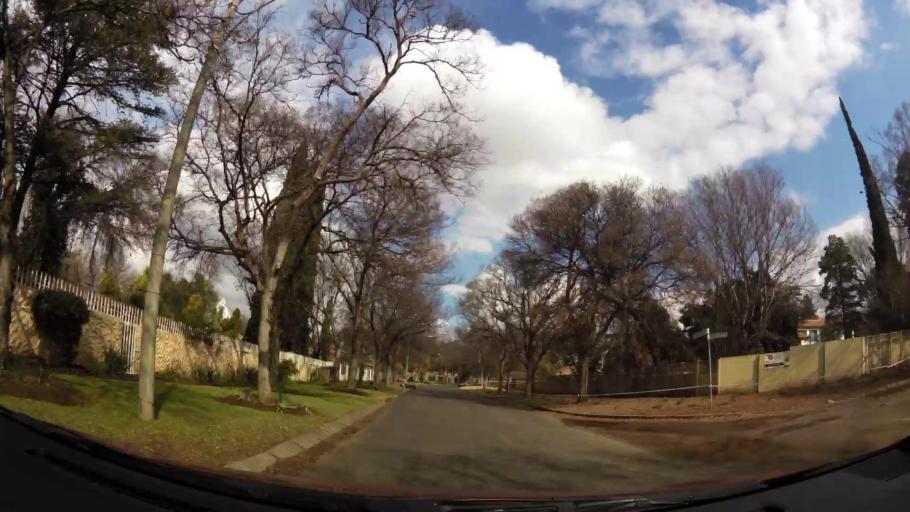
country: ZA
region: Gauteng
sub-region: Sedibeng District Municipality
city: Vanderbijlpark
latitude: -26.7397
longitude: 27.8363
